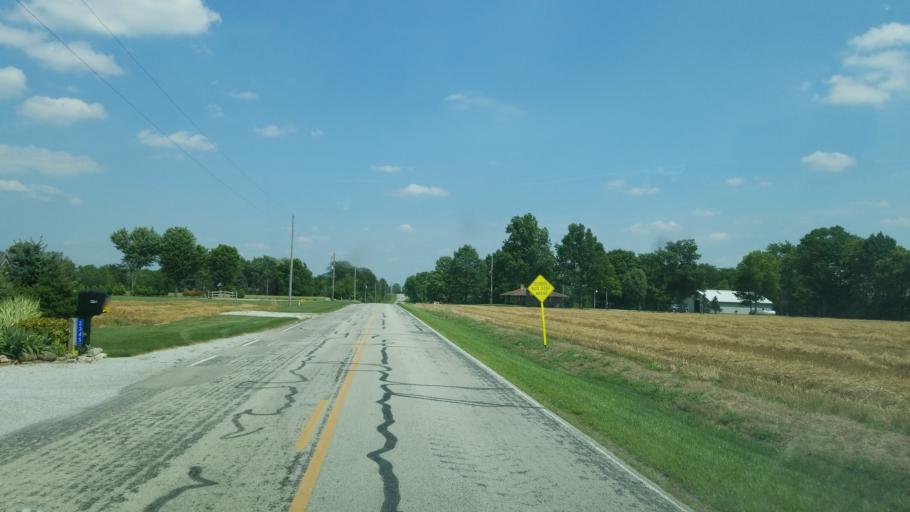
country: US
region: Ohio
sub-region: Seneca County
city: Tiffin
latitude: 41.1383
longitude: -83.2156
